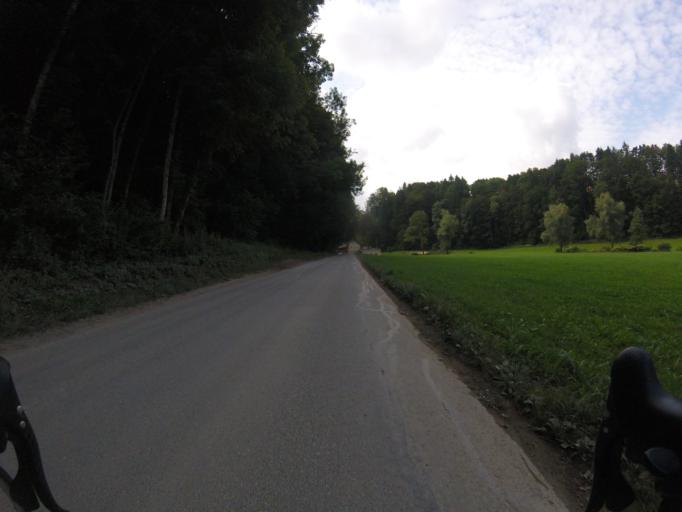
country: CH
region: Bern
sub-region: Emmental District
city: Oberburg
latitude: 47.0324
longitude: 7.6098
